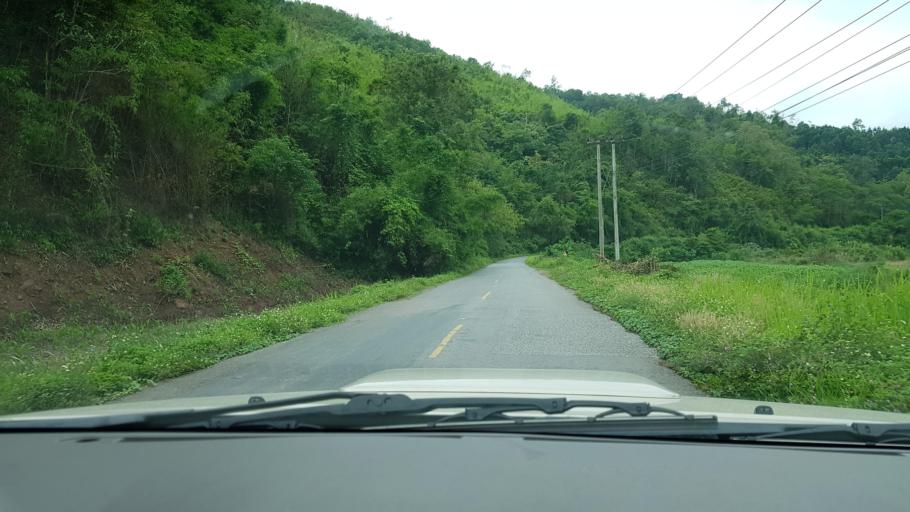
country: LA
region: Loungnamtha
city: Muang Nale
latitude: 20.3729
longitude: 101.7242
